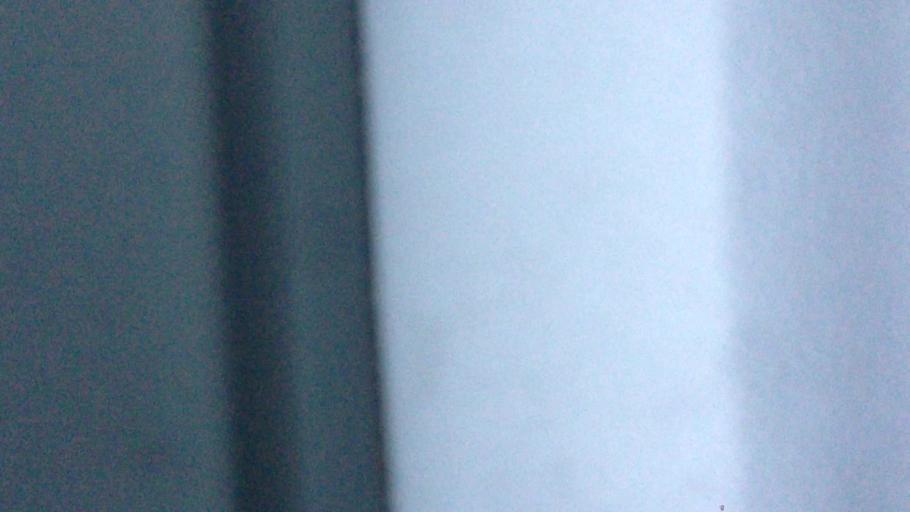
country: US
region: New York
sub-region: Dutchess County
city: Rhinebeck
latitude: 41.9604
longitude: -73.9231
